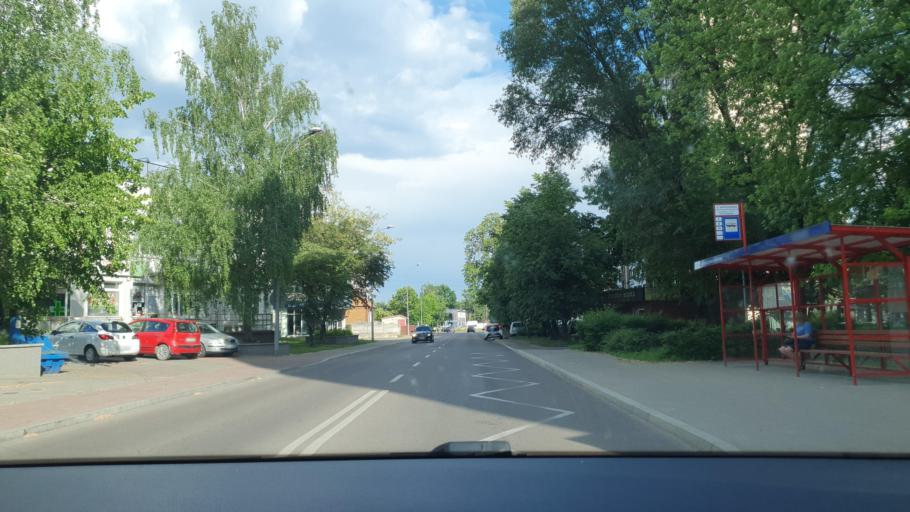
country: PL
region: Podlasie
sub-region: Bialystok
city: Bialystok
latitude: 53.1277
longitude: 23.1809
